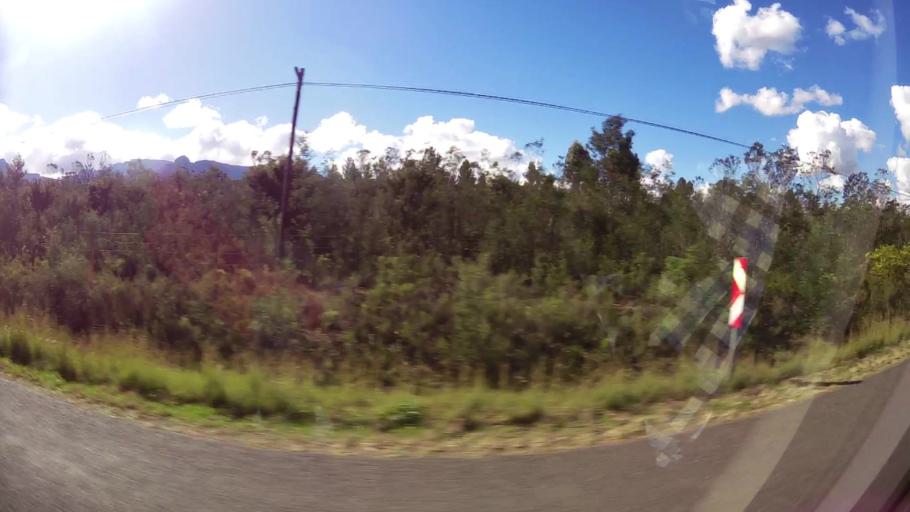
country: ZA
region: Western Cape
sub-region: Overberg District Municipality
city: Swellendam
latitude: -34.0357
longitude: 20.4236
